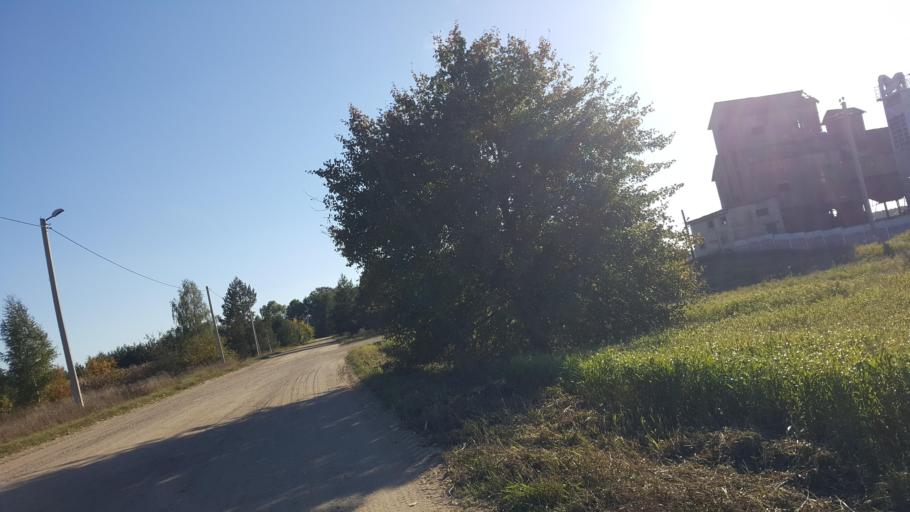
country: BY
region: Brest
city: Kamyanyets
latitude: 52.3955
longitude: 23.8852
